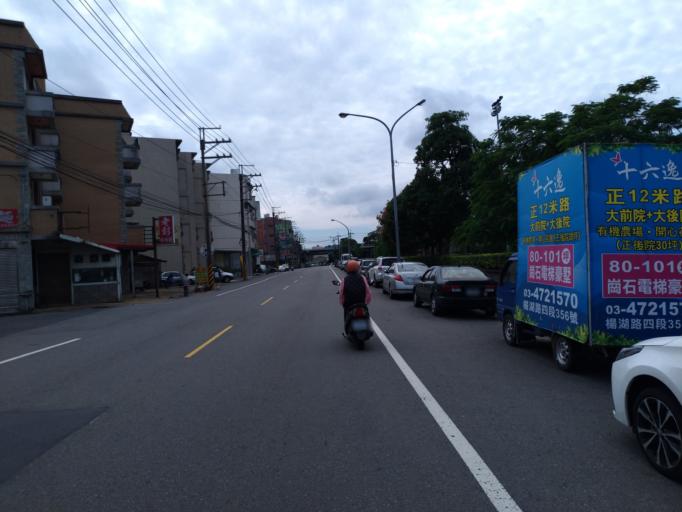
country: TW
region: Taiwan
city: Daxi
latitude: 24.9168
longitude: 121.1449
